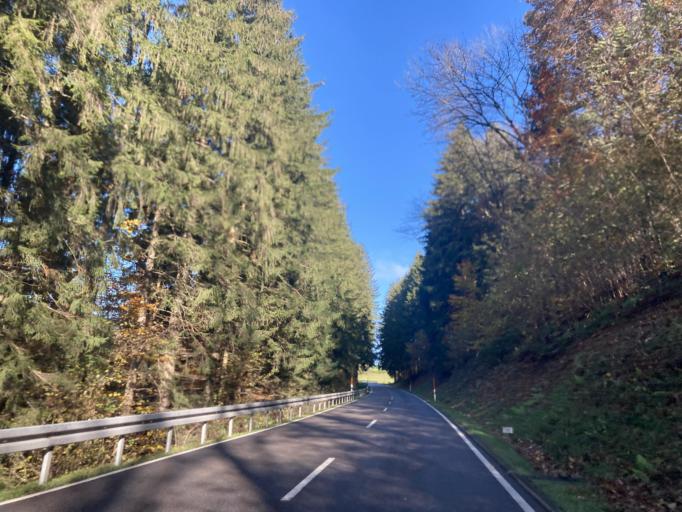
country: DE
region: Baden-Wuerttemberg
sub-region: Freiburg Region
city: Elzach
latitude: 48.2097
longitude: 8.0871
